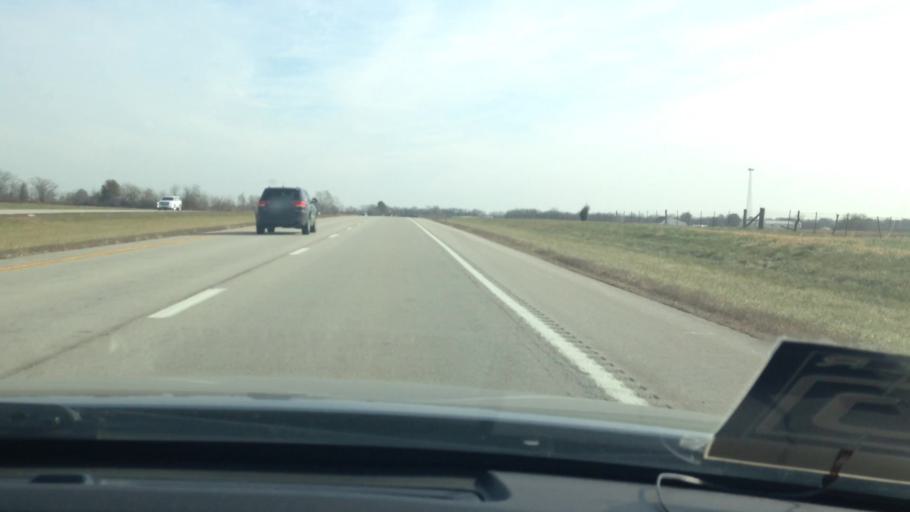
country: US
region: Missouri
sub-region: Cass County
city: Harrisonville
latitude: 38.6094
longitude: -94.3106
